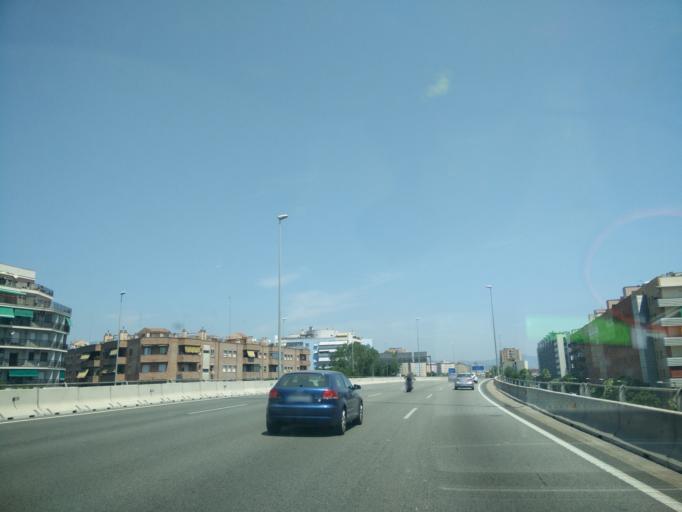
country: ES
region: Catalonia
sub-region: Provincia de Barcelona
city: Sant Adria de Besos
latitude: 41.4274
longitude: 2.2195
